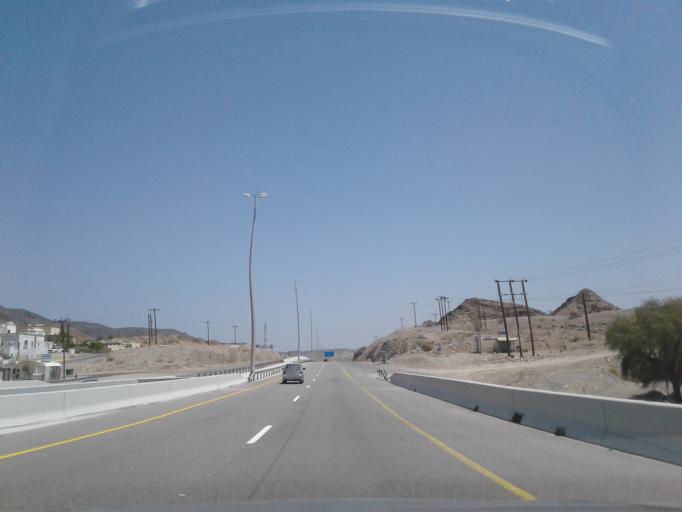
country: OM
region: Muhafazat Masqat
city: Muscat
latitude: 23.2577
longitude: 58.7728
